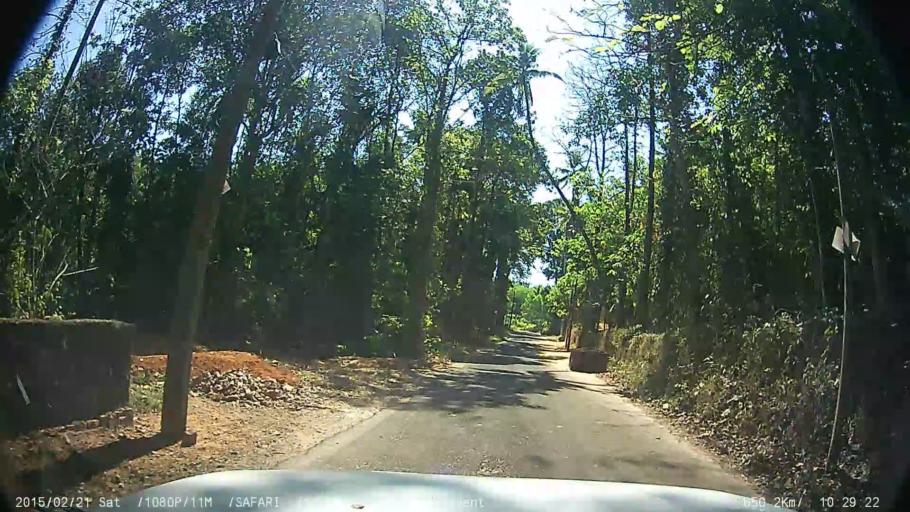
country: IN
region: Kerala
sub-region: Kottayam
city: Palackattumala
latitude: 9.8559
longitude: 76.6964
